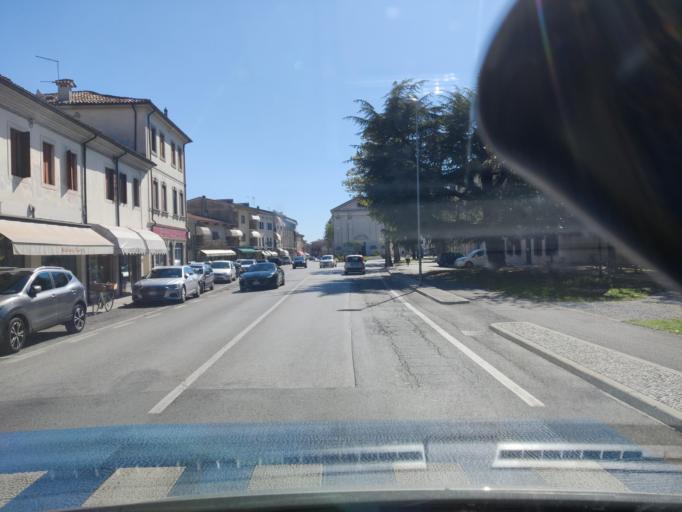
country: IT
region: Veneto
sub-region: Provincia di Treviso
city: Vittorio Veneto
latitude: 45.9643
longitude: 12.3221
